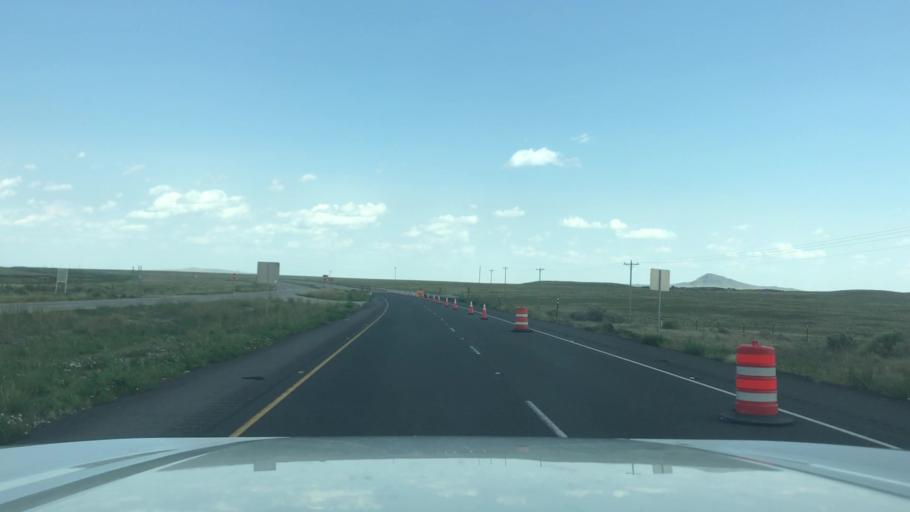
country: US
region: New Mexico
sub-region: Union County
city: Clayton
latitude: 36.6161
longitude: -103.6879
